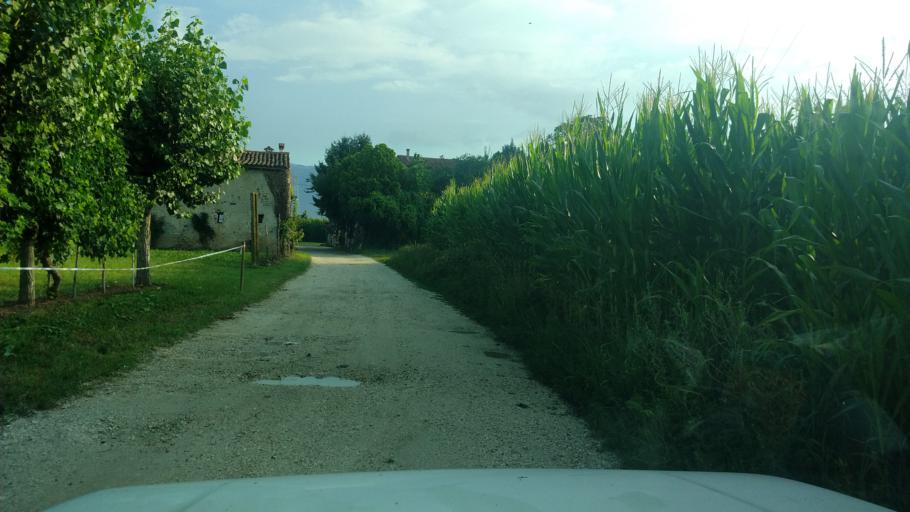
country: IT
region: Veneto
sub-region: Provincia di Vicenza
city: Nove
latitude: 45.7247
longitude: 11.6645
